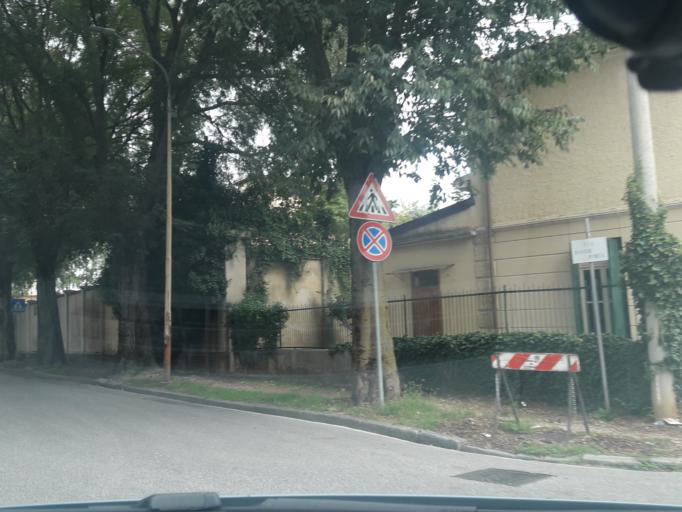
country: IT
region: Friuli Venezia Giulia
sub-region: Provincia di Udine
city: Udine
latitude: 46.0655
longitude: 13.2554
